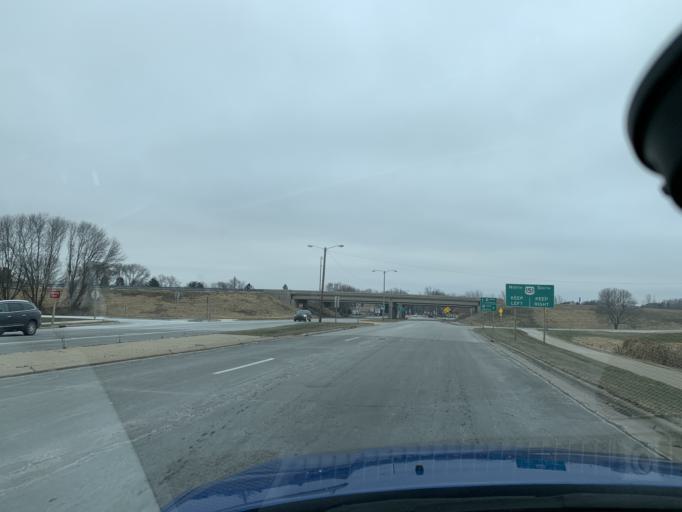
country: US
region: Wisconsin
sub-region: Dane County
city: Sun Prairie
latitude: 43.1985
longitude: -89.2109
